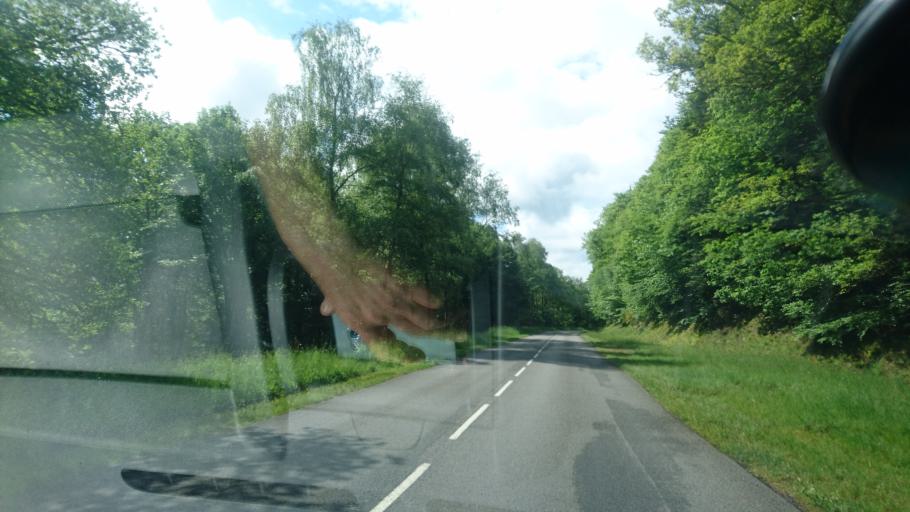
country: FR
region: Limousin
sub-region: Departement de la Haute-Vienne
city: Peyrat-le-Chateau
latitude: 45.7922
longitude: 1.8509
